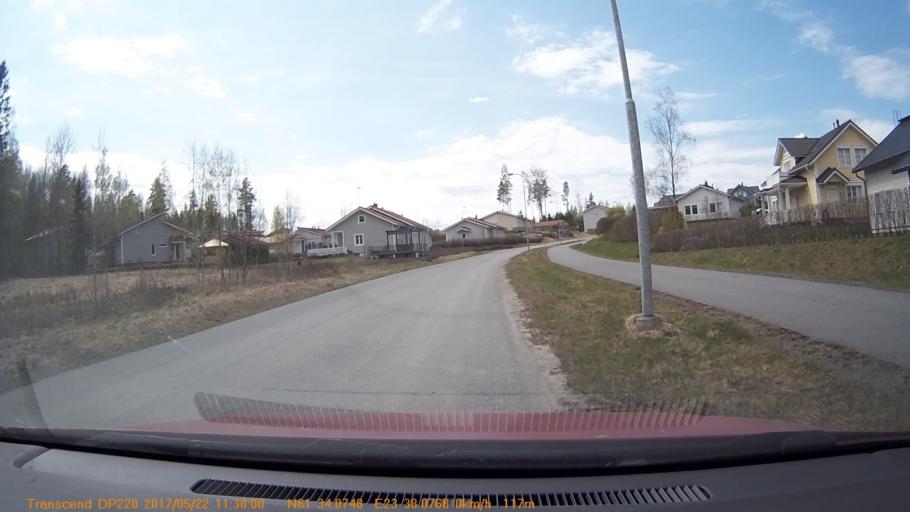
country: FI
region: Pirkanmaa
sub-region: Tampere
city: Yloejaervi
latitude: 61.5679
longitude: 23.6346
